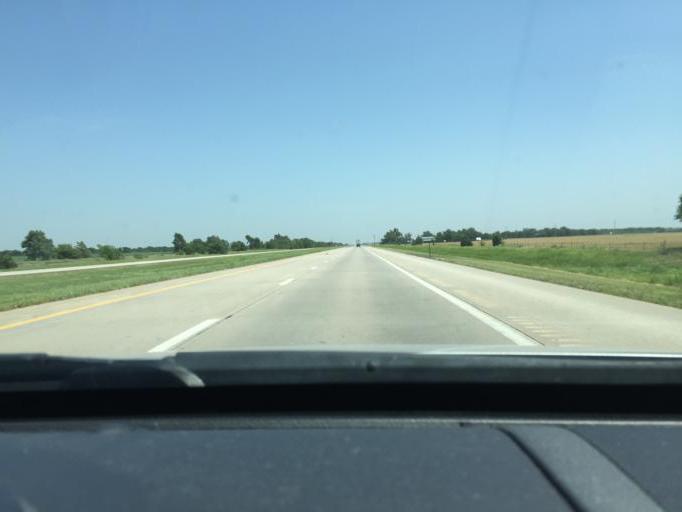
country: US
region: Kansas
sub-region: Reno County
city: South Hutchinson
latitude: 37.9602
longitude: -97.9133
